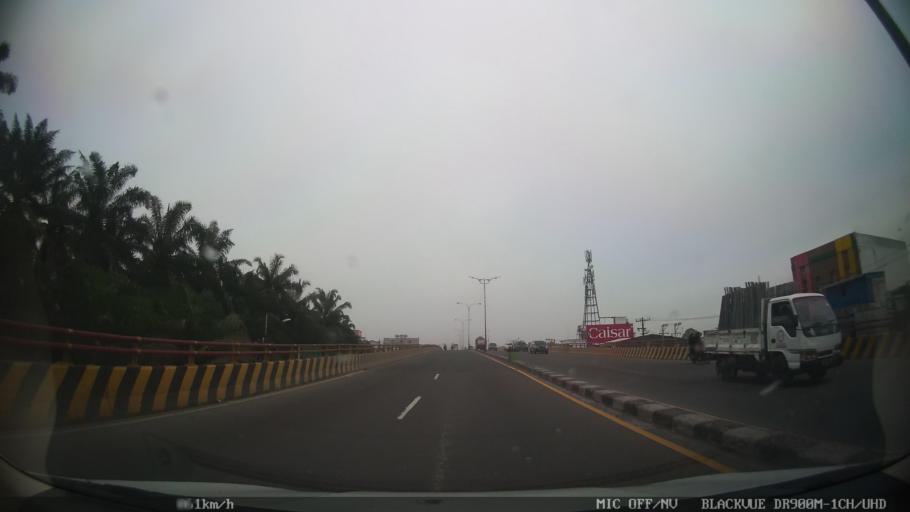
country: ID
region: North Sumatra
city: Deli Tua
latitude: 3.5365
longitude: 98.7158
